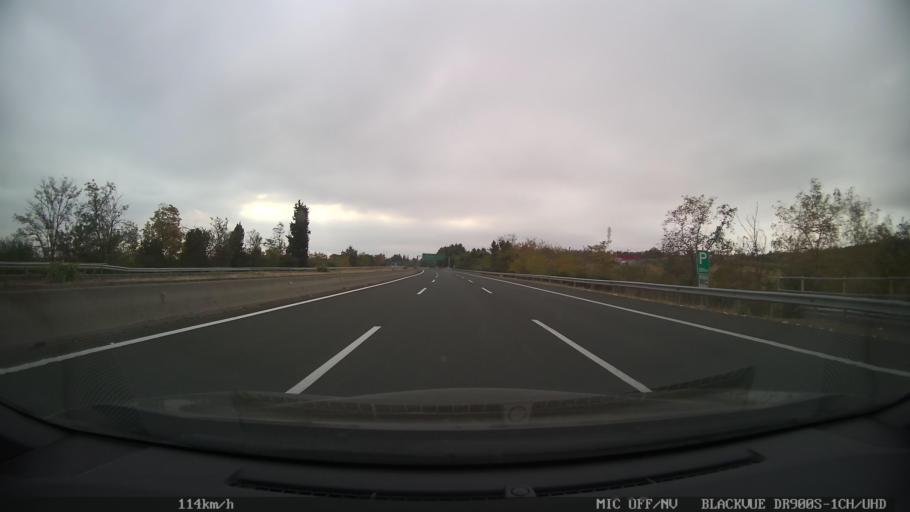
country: GR
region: Central Macedonia
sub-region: Nomos Pierias
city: Aiginio
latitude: 40.4730
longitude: 22.5718
